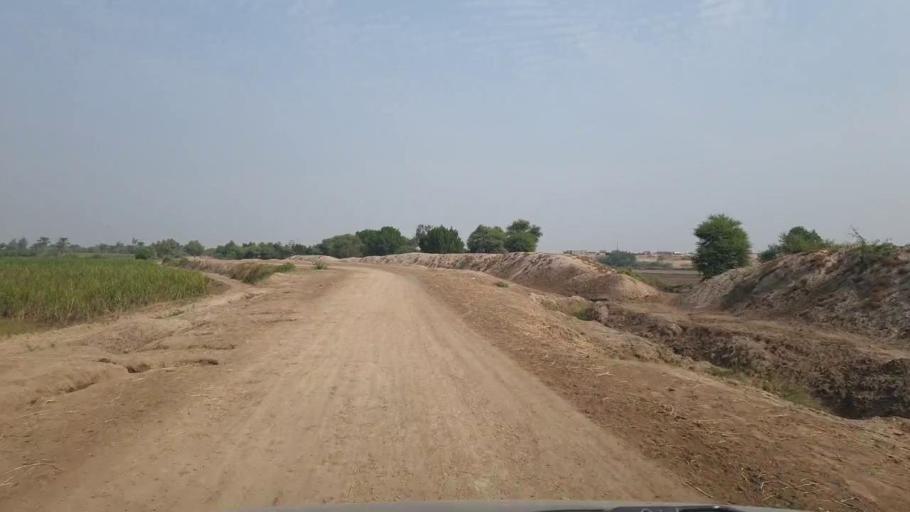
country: PK
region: Sindh
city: Tando Muhammad Khan
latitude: 25.1551
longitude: 68.4673
